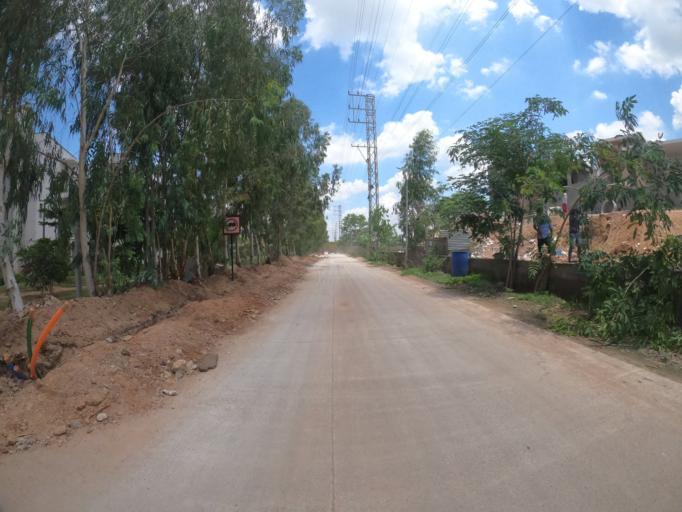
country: IN
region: Telangana
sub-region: Medak
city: Serilingampalle
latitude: 17.3828
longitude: 78.3250
